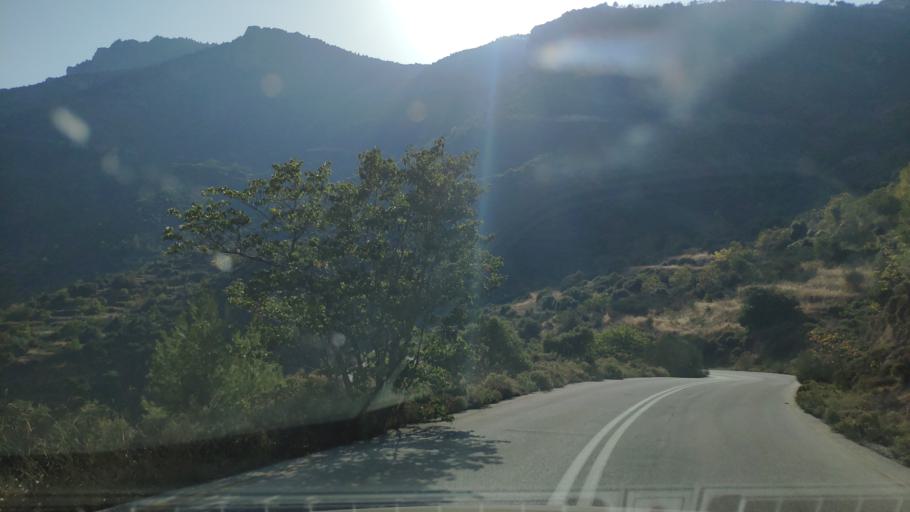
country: GR
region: West Greece
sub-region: Nomos Achaias
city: Aiyira
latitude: 38.0682
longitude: 22.3850
